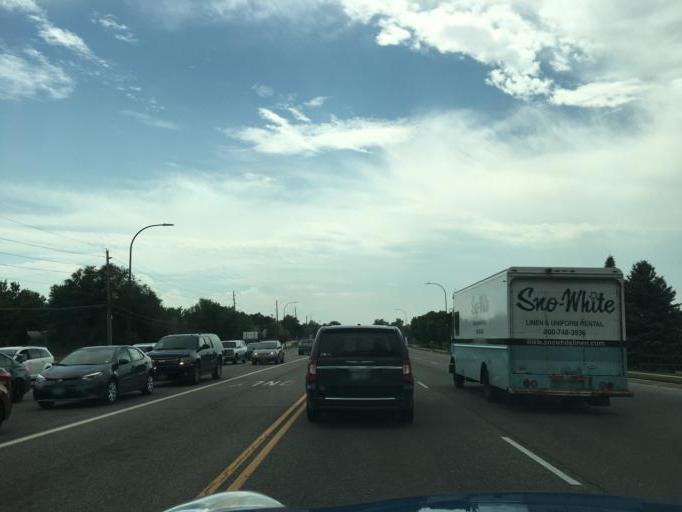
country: US
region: Colorado
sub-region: Jefferson County
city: Arvada
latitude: 39.8376
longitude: -105.0818
